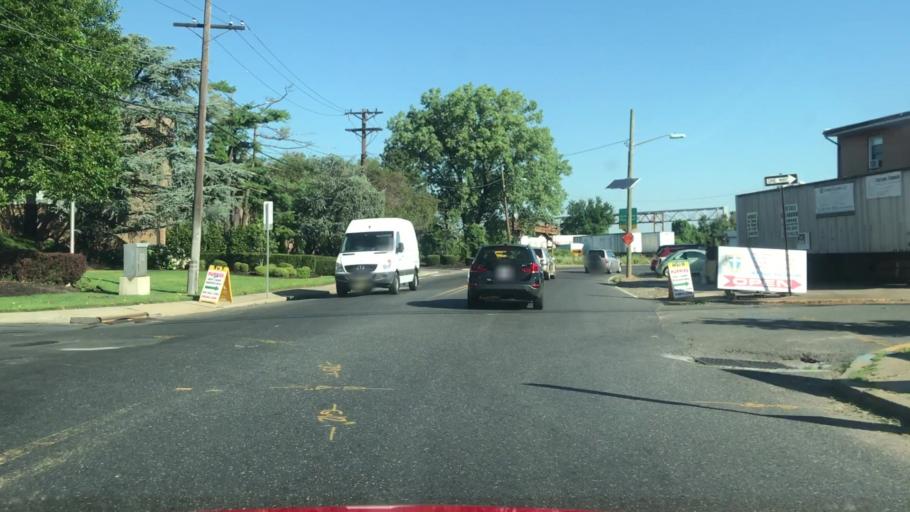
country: US
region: New Jersey
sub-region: Bergen County
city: Ridgefield
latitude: 40.8359
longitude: -74.0178
